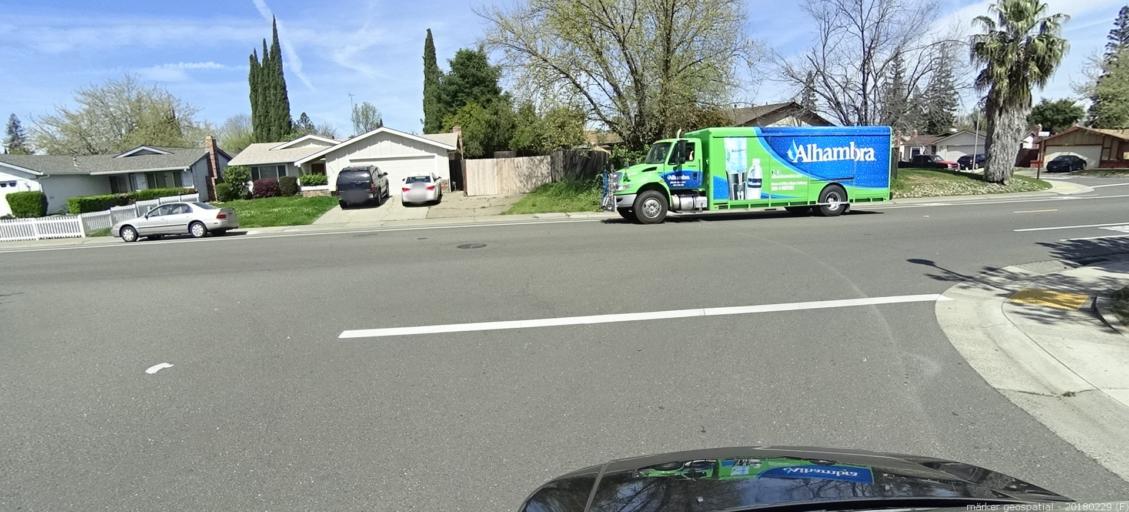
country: US
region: California
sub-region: Sacramento County
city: La Riviera
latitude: 38.5544
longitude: -121.3473
